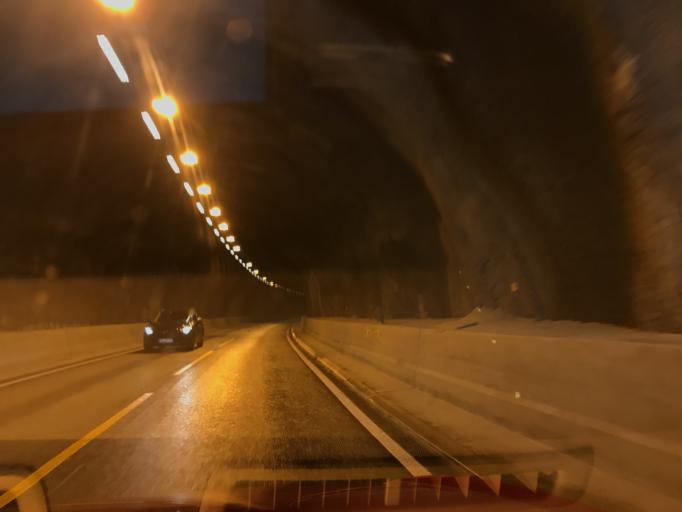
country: NO
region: Vest-Agder
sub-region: Mandal
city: Mandal
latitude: 58.0308
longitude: 7.4681
